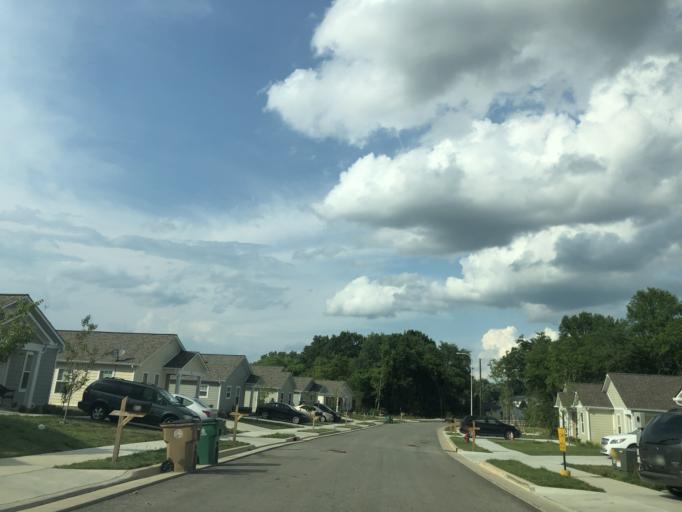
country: US
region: Tennessee
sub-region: Davidson County
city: Nashville
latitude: 36.2282
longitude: -86.7977
